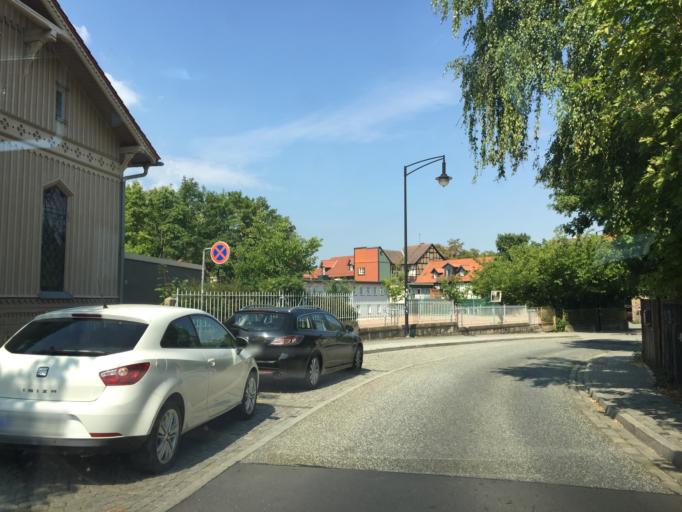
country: DE
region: Saxony-Anhalt
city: Wernigerode
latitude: 51.8318
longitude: 10.7827
